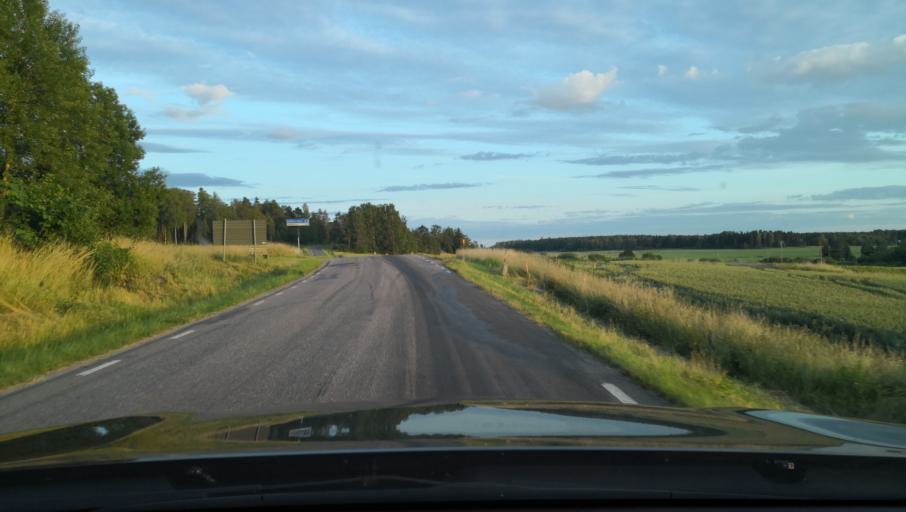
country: SE
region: Uppsala
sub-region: Uppsala Kommun
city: Vattholma
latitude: 60.0176
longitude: 17.7206
